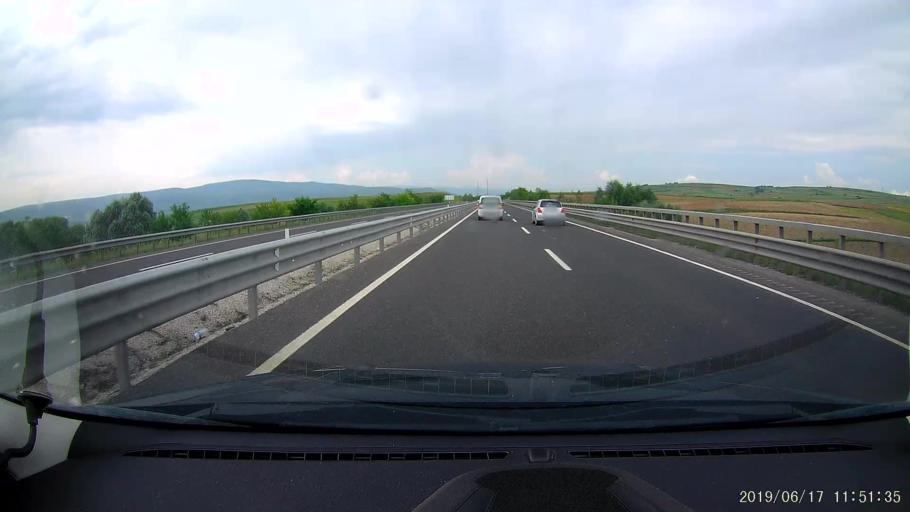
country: TR
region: Cankiri
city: Atkaracalar
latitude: 40.8166
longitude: 33.1024
